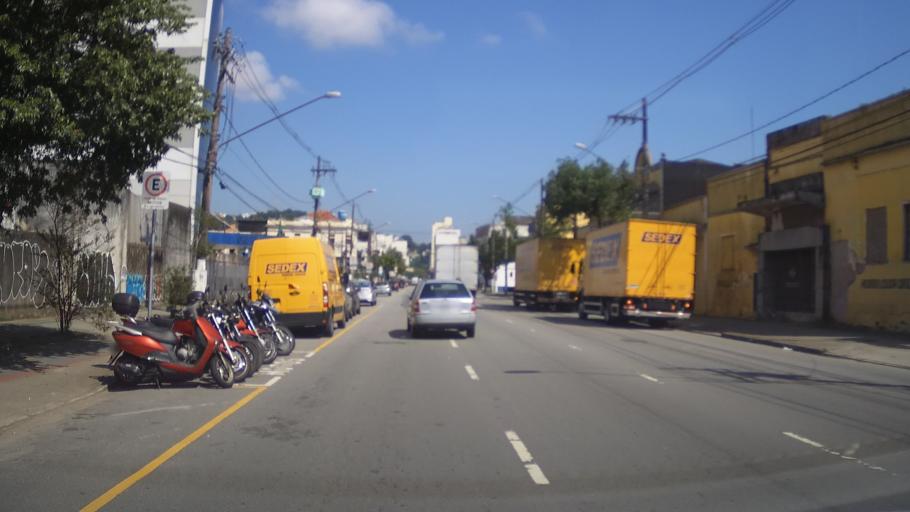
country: BR
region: Sao Paulo
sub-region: Santos
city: Santos
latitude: -23.9362
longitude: -46.3211
